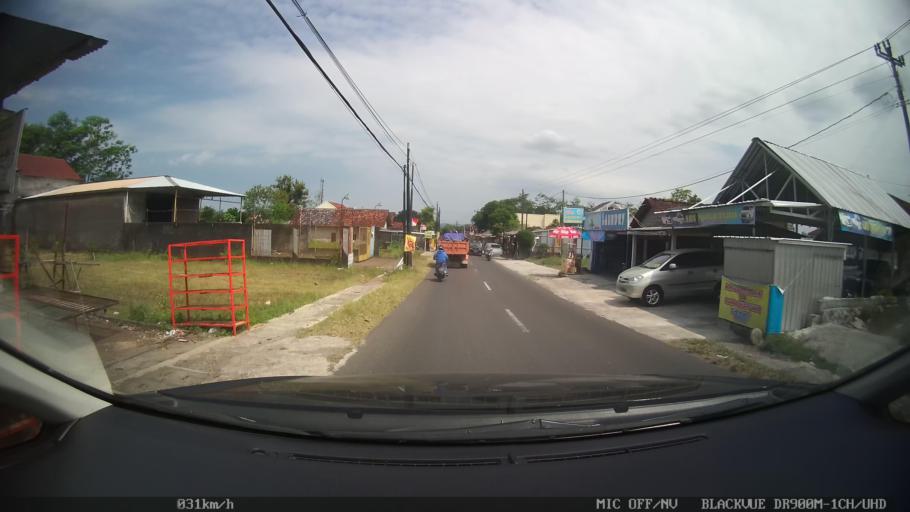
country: ID
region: Daerah Istimewa Yogyakarta
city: Depok
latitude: -7.7356
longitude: 110.4516
